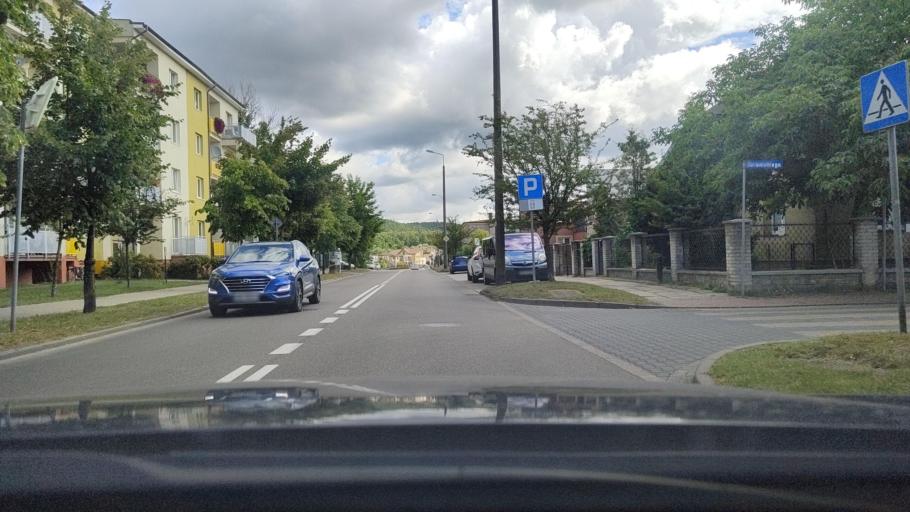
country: PL
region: Pomeranian Voivodeship
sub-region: Powiat wejherowski
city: Wejherowo
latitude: 54.6099
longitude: 18.2266
